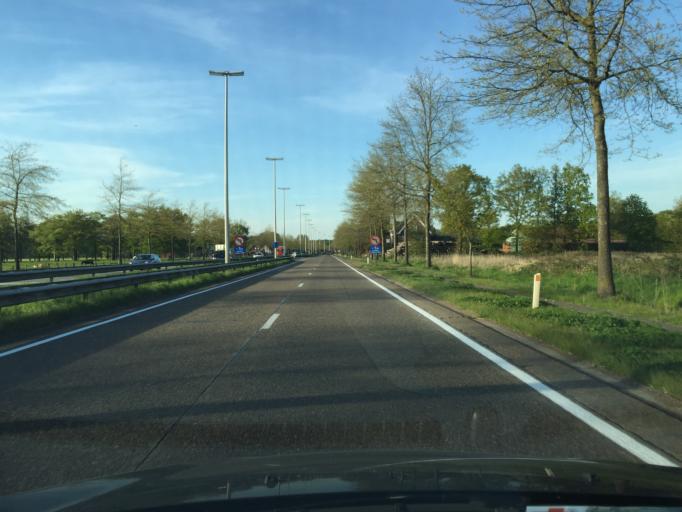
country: BE
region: Flanders
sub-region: Provincie Oost-Vlaanderen
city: Knesselare
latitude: 51.1578
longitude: 3.4358
